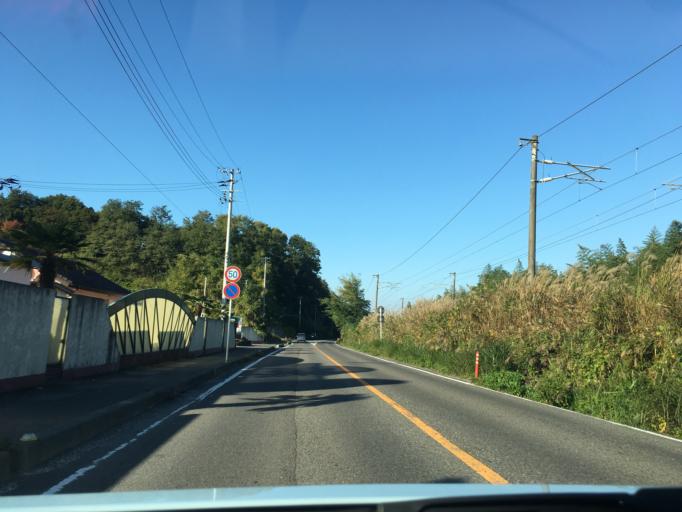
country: JP
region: Fukushima
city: Sukagawa
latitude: 37.3150
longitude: 140.3779
